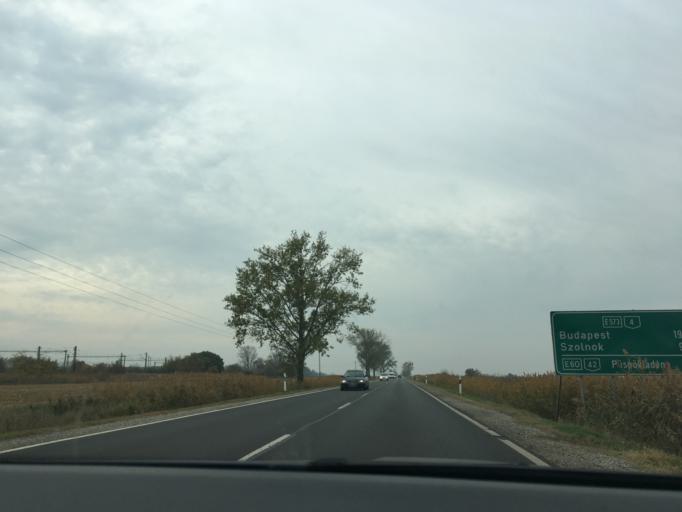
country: HU
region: Hajdu-Bihar
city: Kaba
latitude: 47.3653
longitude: 21.2486
